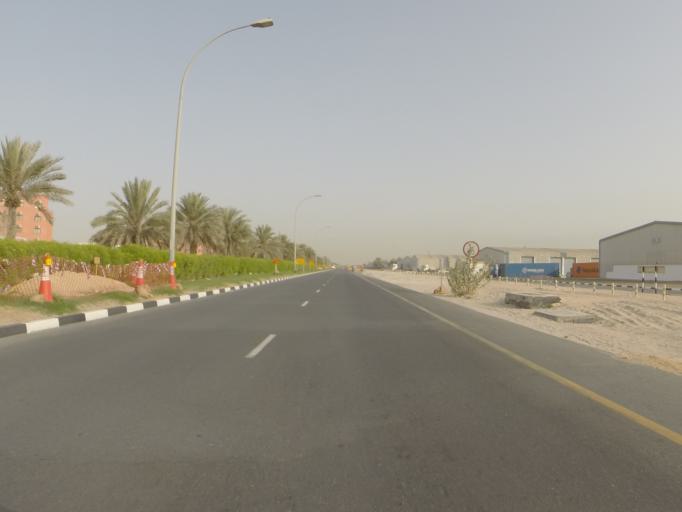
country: AE
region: Dubai
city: Dubai
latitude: 24.9582
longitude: 55.0606
